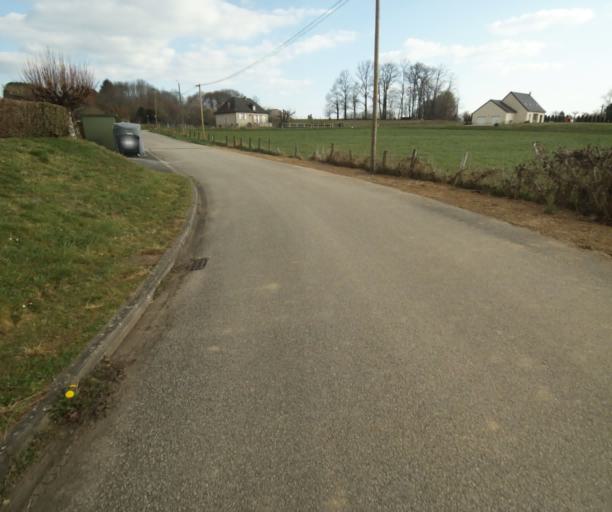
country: FR
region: Limousin
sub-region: Departement de la Correze
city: Saint-Clement
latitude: 45.3510
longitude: 1.6336
